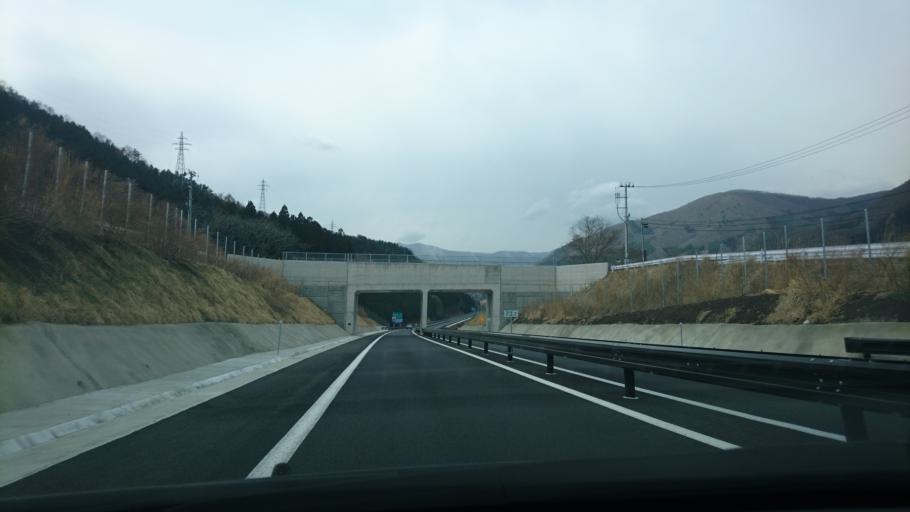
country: JP
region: Iwate
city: Kamaishi
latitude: 39.2513
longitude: 141.7890
